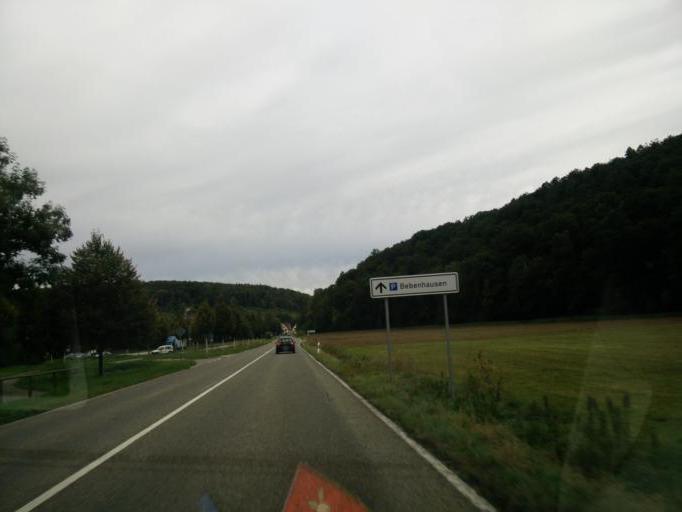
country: DE
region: Baden-Wuerttemberg
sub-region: Tuebingen Region
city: Tuebingen
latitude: 48.5564
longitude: 9.0664
